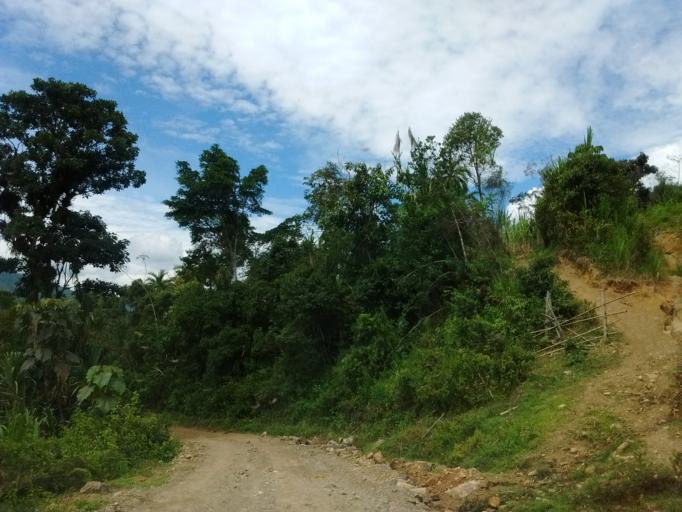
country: CO
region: Cauca
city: Morales
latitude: 2.6858
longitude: -76.7611
